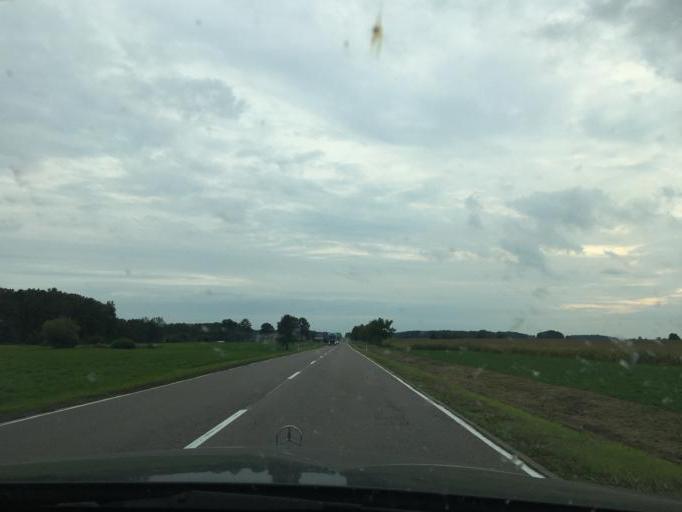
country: PL
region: Podlasie
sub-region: Powiat lomzynski
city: Sniadowo
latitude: 52.9806
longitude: 21.9005
